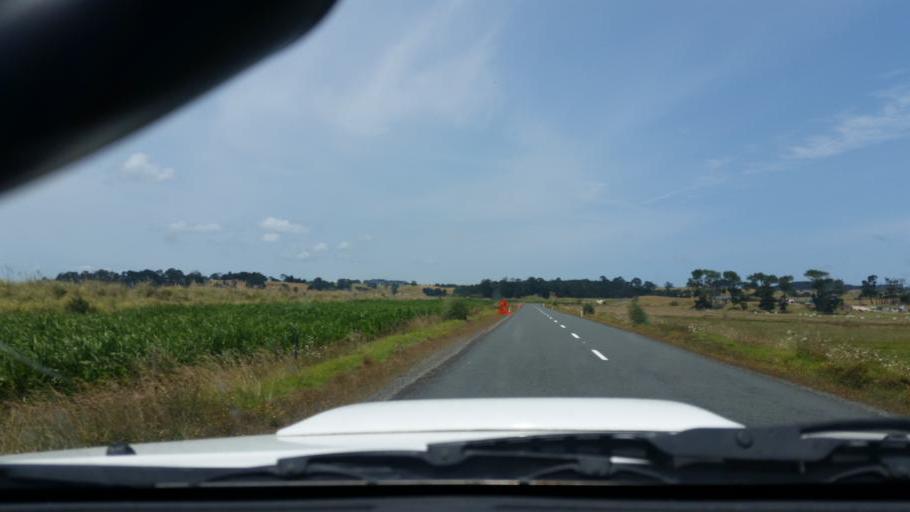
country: NZ
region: Northland
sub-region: Kaipara District
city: Dargaville
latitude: -36.1802
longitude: 174.0304
